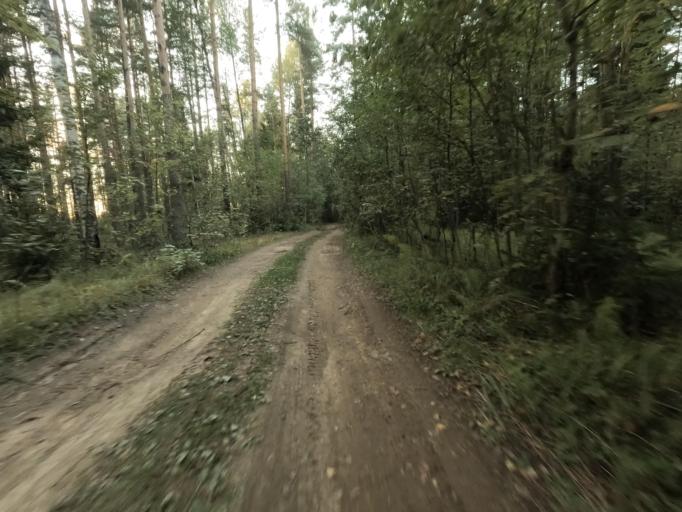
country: RU
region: Leningrad
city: Otradnoye
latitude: 59.8392
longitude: 30.8042
